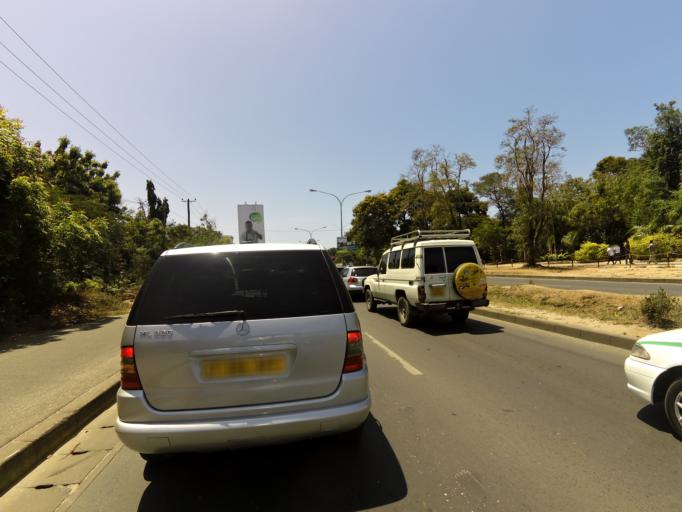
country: TZ
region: Dar es Salaam
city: Magomeni
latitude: -6.7848
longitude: 39.2767
